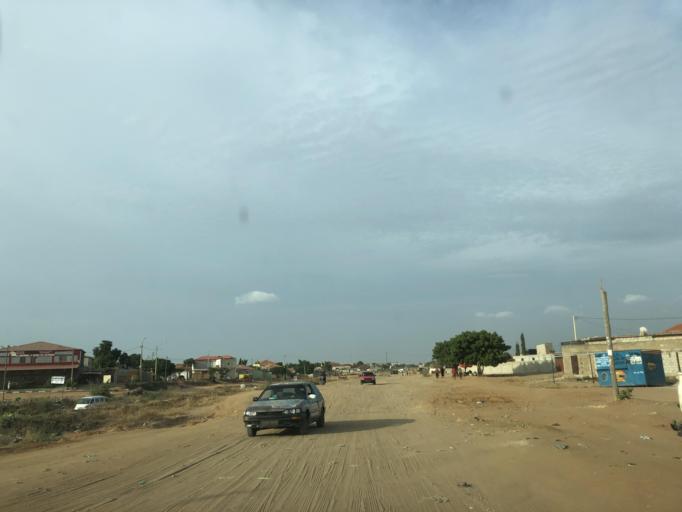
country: AO
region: Luanda
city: Luanda
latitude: -8.9225
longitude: 13.3074
